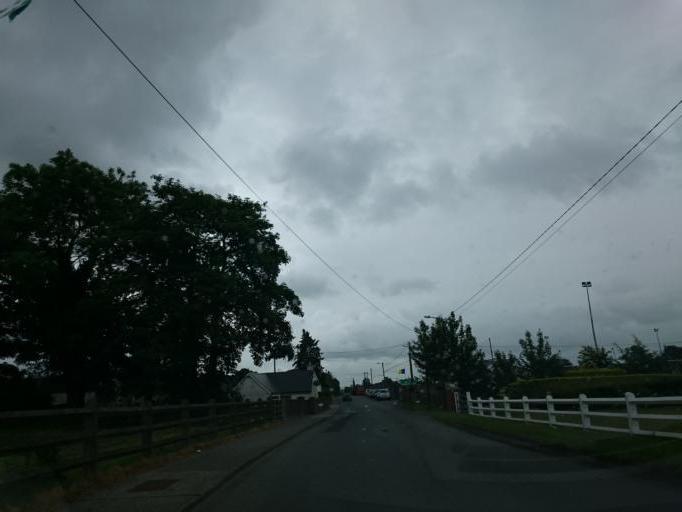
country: IE
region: Leinster
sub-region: Wicklow
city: Baltinglass
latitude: 52.9328
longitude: -6.6848
